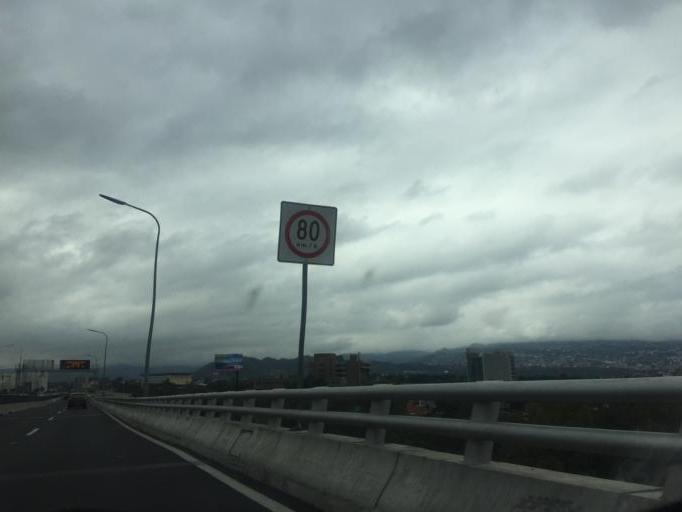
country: MX
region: Mexico City
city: Tlalpan
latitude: 19.2947
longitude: -99.1551
